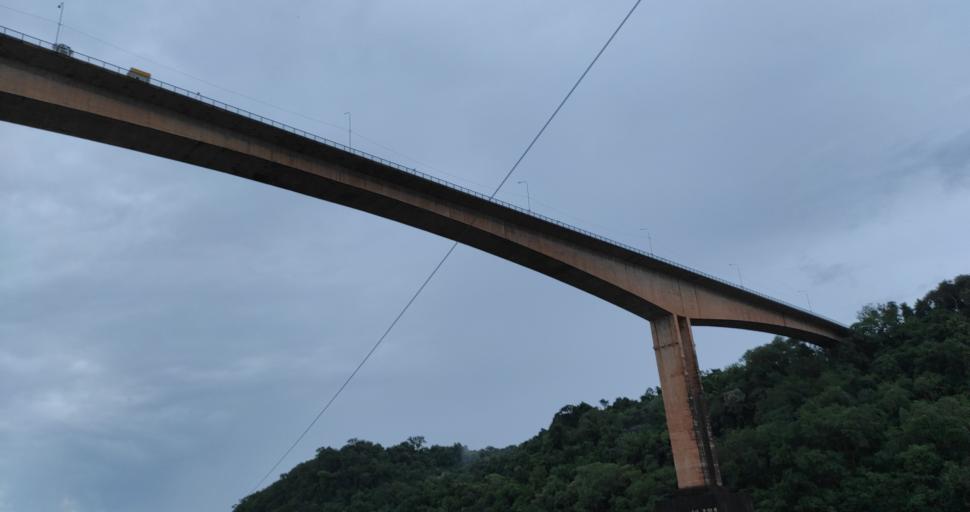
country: AR
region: Misiones
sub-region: Departamento de Iguazu
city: Puerto Iguazu
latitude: -25.5888
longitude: -54.5604
